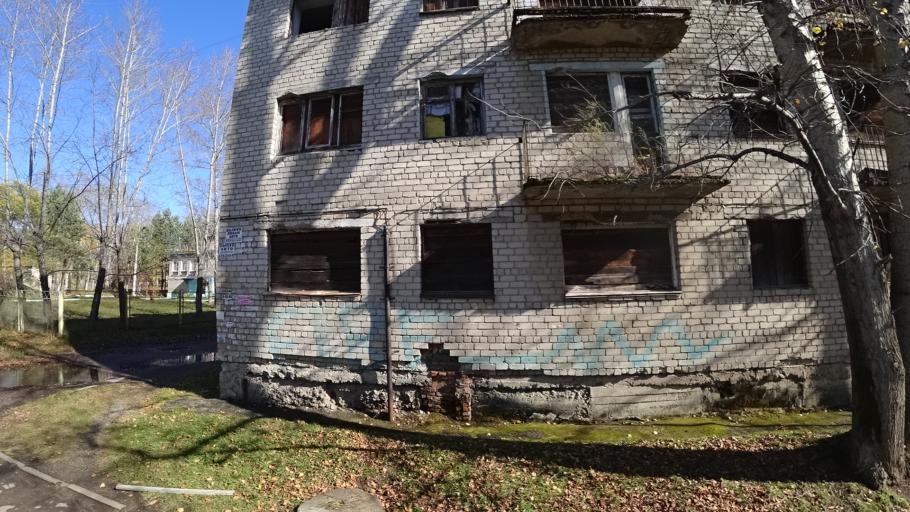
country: RU
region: Khabarovsk Krai
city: Amursk
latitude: 50.2163
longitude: 136.9013
